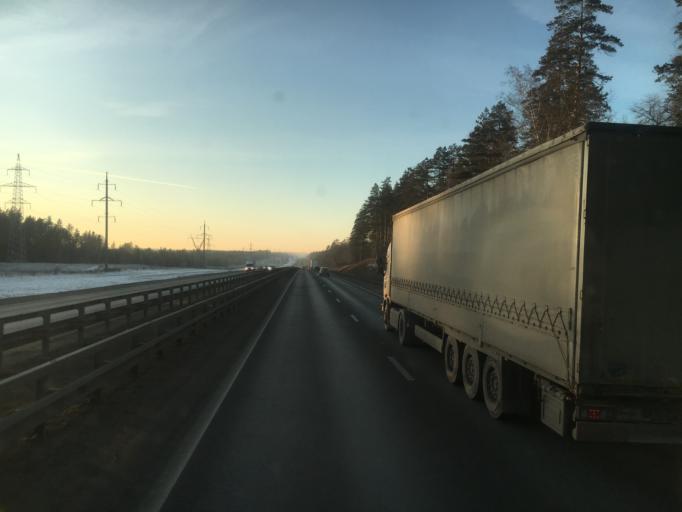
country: RU
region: Samara
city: Povolzhskiy
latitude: 53.5179
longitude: 49.7857
